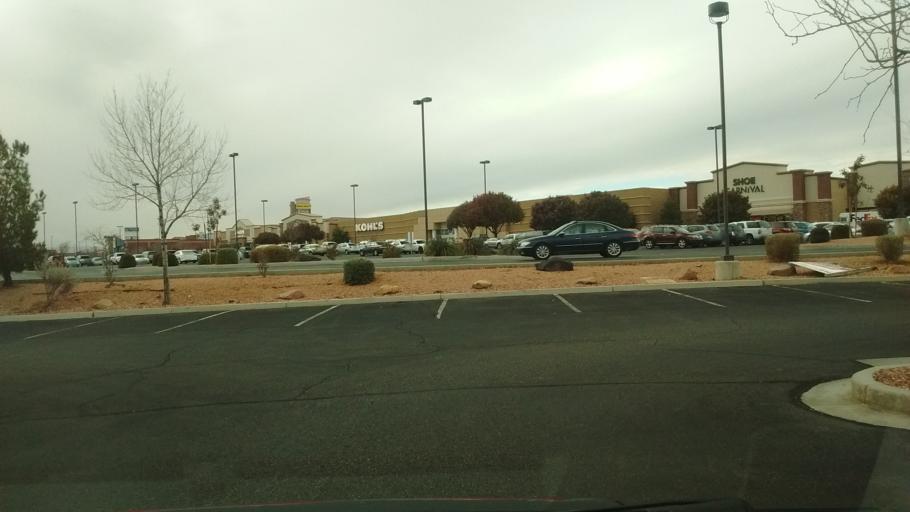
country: US
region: Utah
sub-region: Washington County
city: Washington
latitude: 37.1299
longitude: -113.5195
